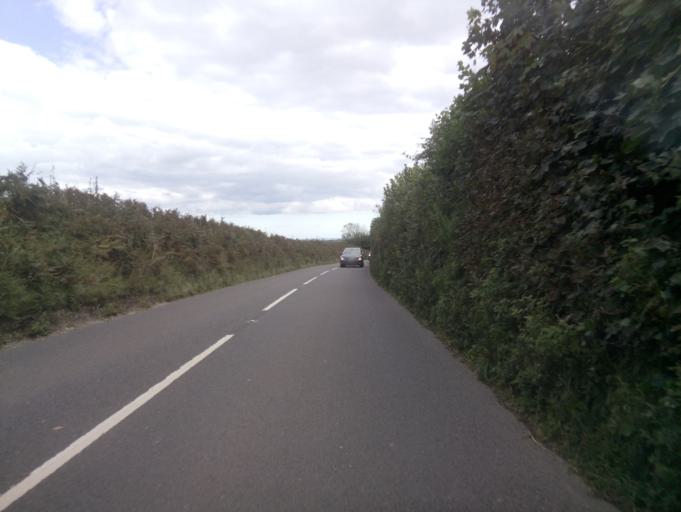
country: GB
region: England
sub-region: Devon
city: Dartmouth
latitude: 50.3550
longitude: -3.6389
